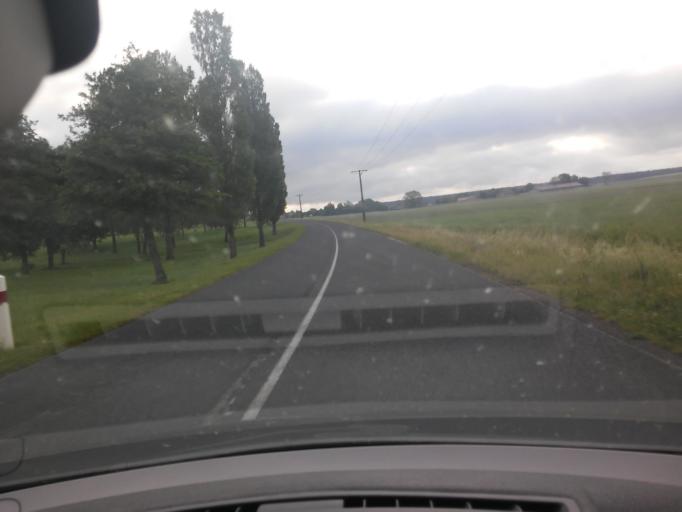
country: FR
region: Lorraine
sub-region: Departement de la Meuse
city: Vigneulles-les-Hattonchatel
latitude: 48.9841
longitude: 5.7711
